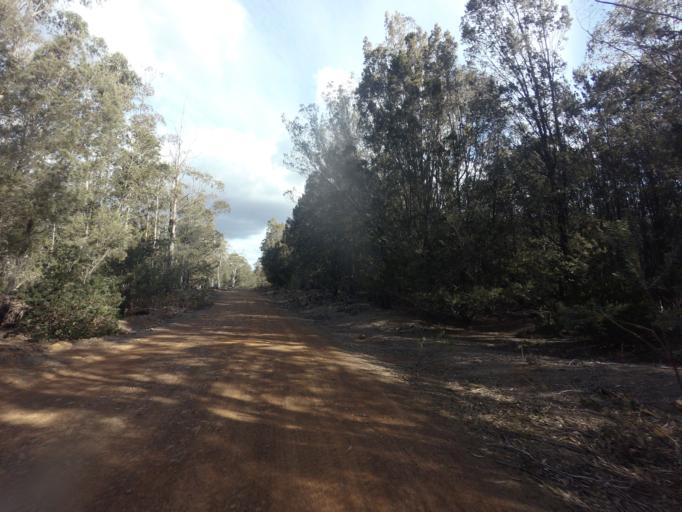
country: AU
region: Tasmania
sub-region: Break O'Day
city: St Helens
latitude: -41.8418
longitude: 148.0867
